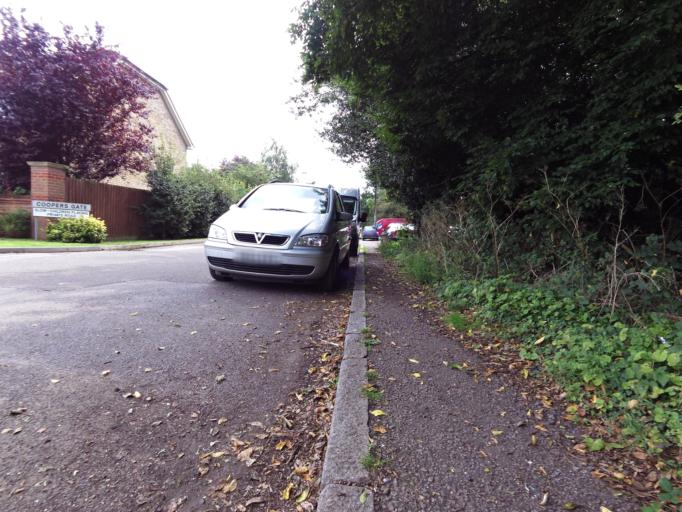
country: GB
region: England
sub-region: Hertfordshire
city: Hatfield
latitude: 51.7406
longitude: -0.2666
